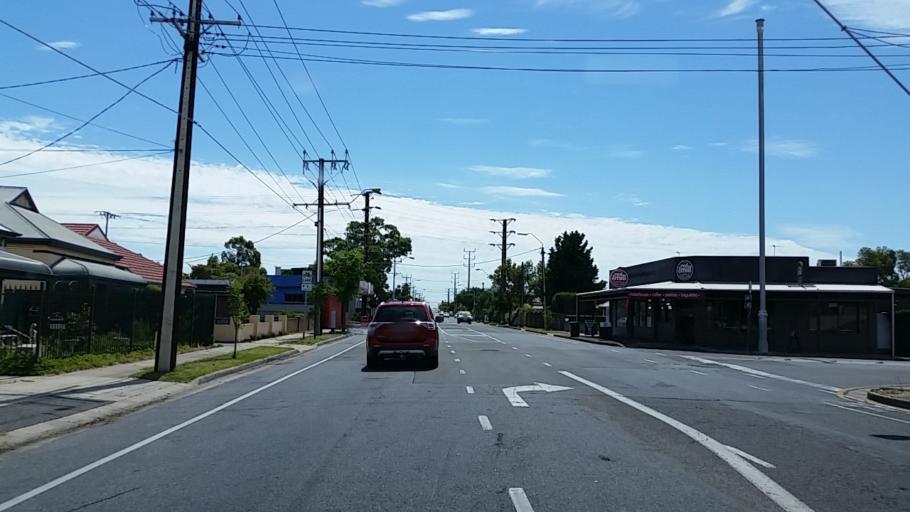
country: AU
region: South Australia
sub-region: Charles Sturt
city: West Lakes Shore
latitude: -34.8514
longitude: 138.4895
